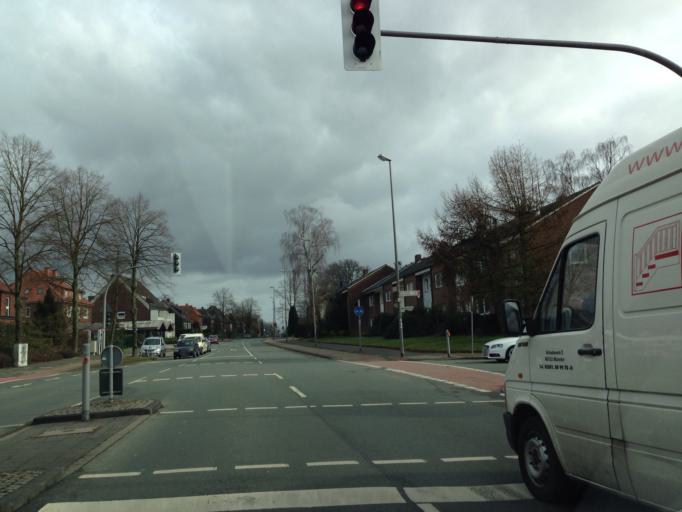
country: DE
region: North Rhine-Westphalia
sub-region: Regierungsbezirk Munster
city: Muenster
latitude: 51.9938
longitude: 7.6073
